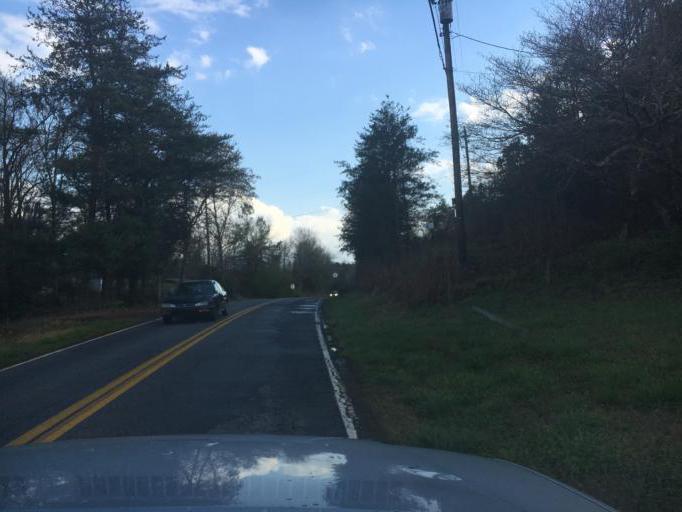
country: US
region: South Carolina
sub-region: Greenville County
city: Parker
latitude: 34.8400
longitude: -82.4945
